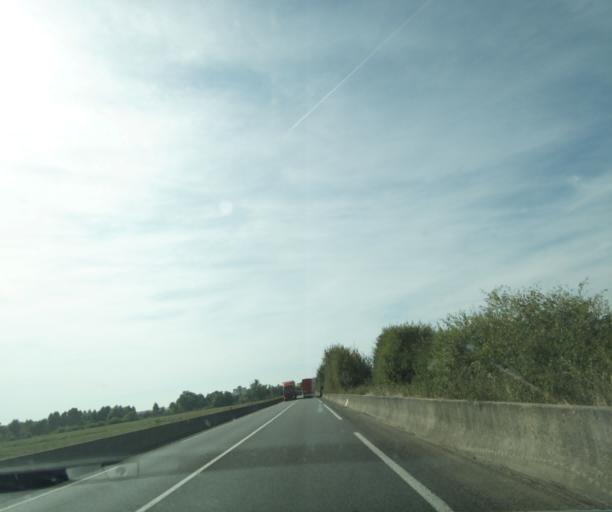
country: FR
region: Auvergne
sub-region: Departement de l'Allier
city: Saint-Remy-en-Rollat
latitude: 46.1891
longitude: 3.4066
